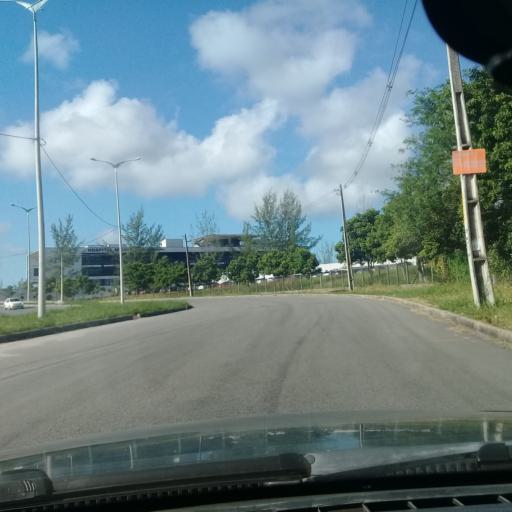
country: BR
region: Pernambuco
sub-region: Abreu E Lima
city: Abreu e Lima
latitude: -7.9219
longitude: -34.8923
